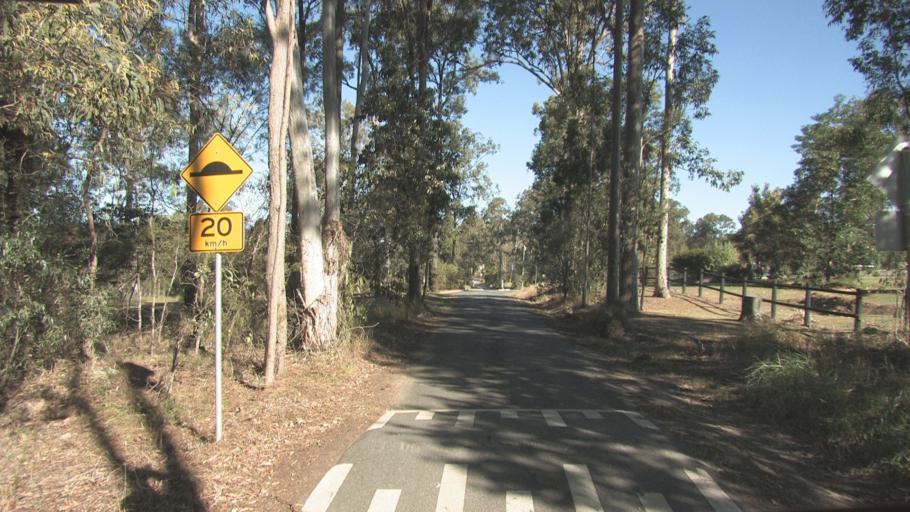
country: AU
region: Queensland
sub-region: Ipswich
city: Springfield Lakes
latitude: -27.7368
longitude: 152.9222
